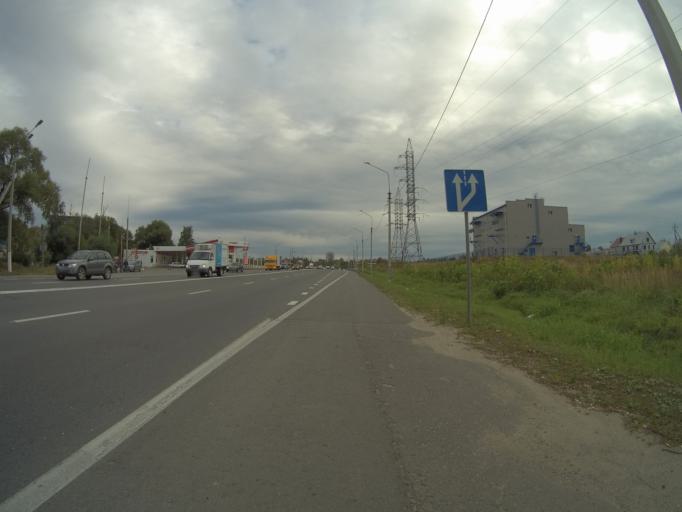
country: RU
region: Vladimir
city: Vladimir
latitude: 56.1212
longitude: 40.3416
